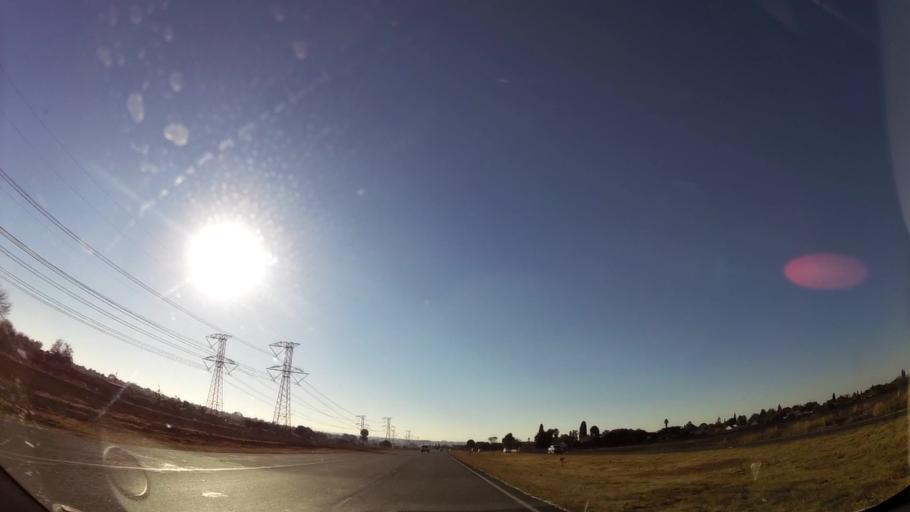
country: ZA
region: Gauteng
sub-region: City of Johannesburg Metropolitan Municipality
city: Modderfontein
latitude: -26.0882
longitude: 28.1940
